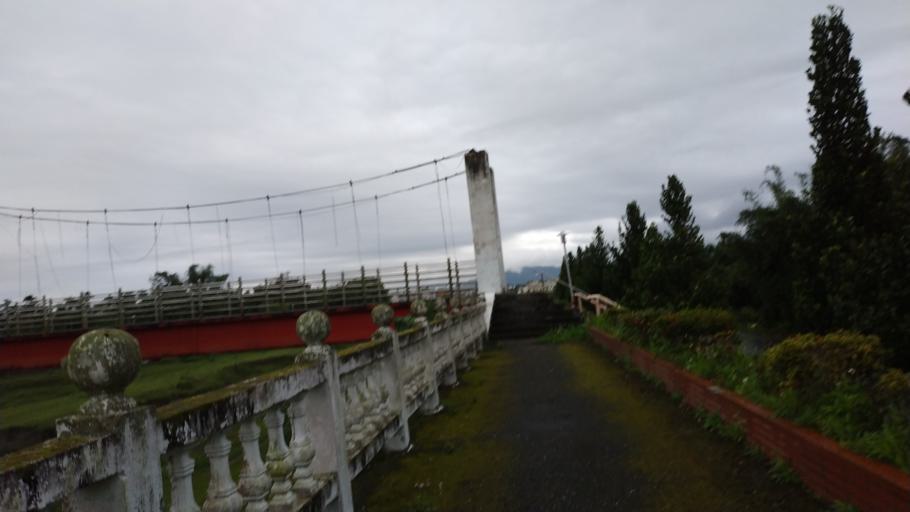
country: TW
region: Taiwan
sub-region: Hualien
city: Hualian
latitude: 23.6620
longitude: 121.4246
